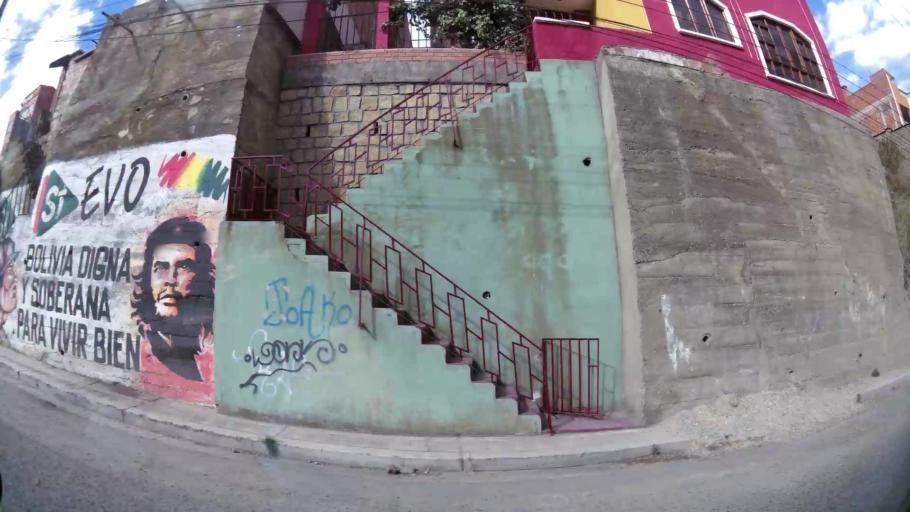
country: BO
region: La Paz
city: La Paz
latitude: -16.4690
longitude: -68.1518
